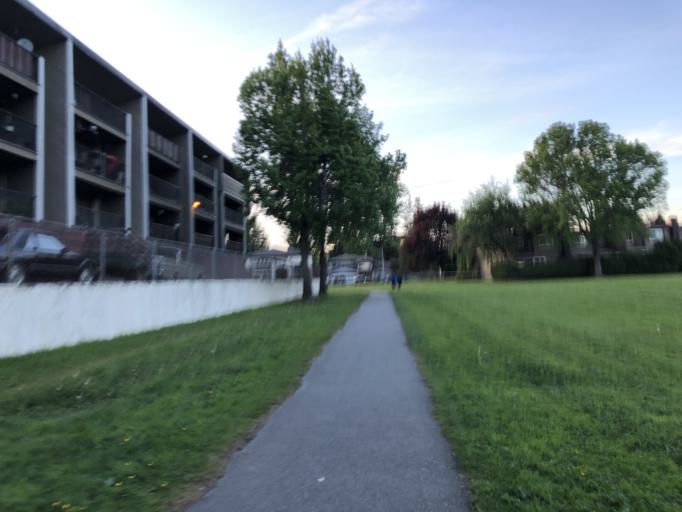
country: CA
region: British Columbia
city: Richmond
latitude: 49.1456
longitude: -123.1216
